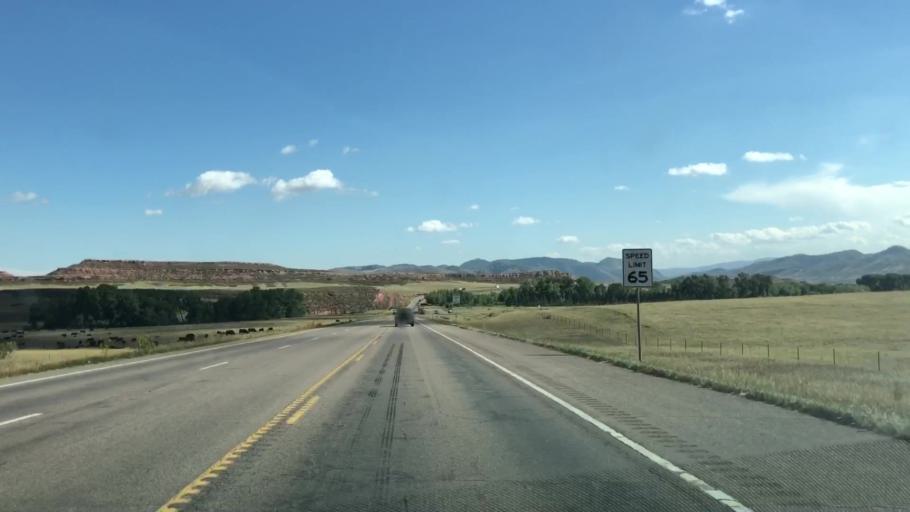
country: US
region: Colorado
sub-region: Larimer County
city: Laporte
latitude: 40.8320
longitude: -105.2459
